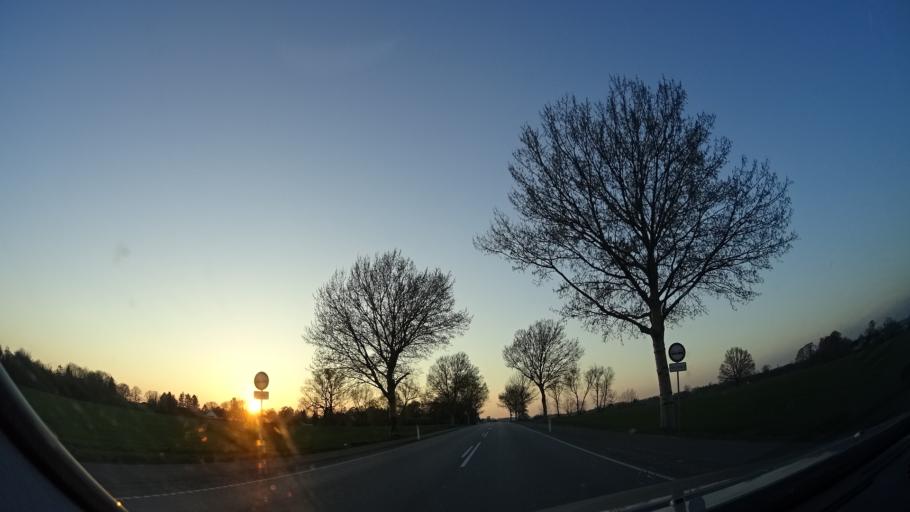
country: DK
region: Zealand
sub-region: Solrod Kommune
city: Solrod
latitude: 55.5509
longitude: 12.1631
